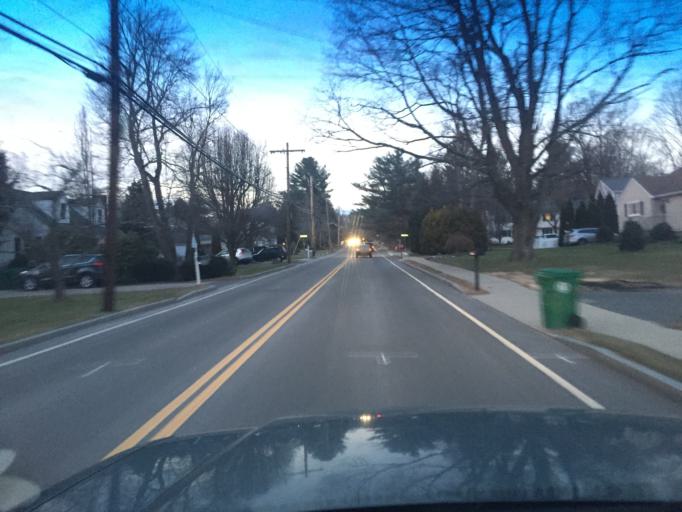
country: US
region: Massachusetts
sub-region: Norfolk County
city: Westwood
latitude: 42.2018
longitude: -71.2194
